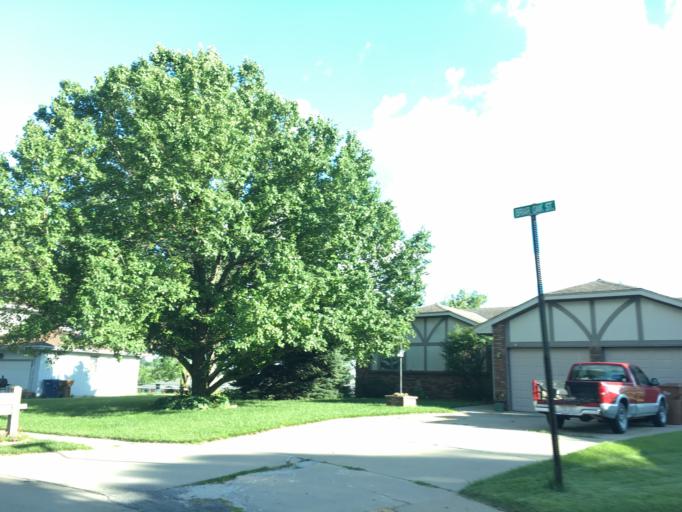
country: US
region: Nebraska
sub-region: Sarpy County
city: Offutt Air Force Base
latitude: 41.1624
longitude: -95.9656
